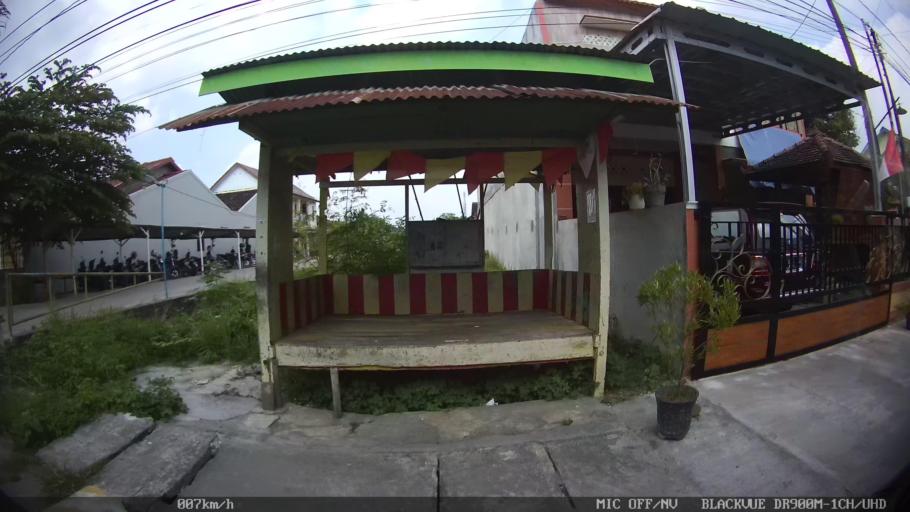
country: ID
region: Daerah Istimewa Yogyakarta
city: Yogyakarta
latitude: -7.8172
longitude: 110.4041
